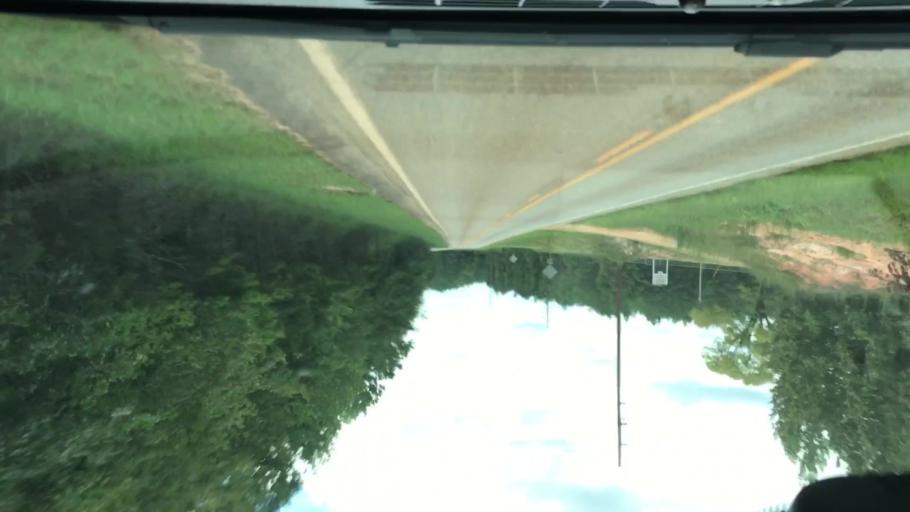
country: US
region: Georgia
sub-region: Stewart County
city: Lumpkin
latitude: 32.0715
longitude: -84.8681
